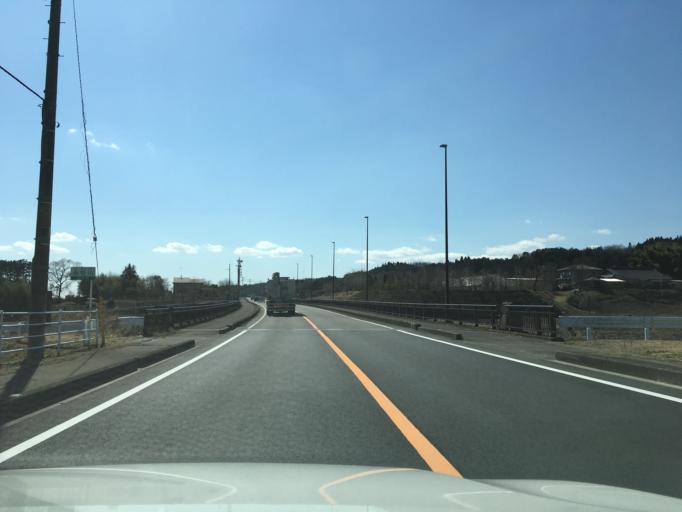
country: JP
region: Tochigi
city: Kuroiso
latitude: 36.9421
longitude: 140.1412
